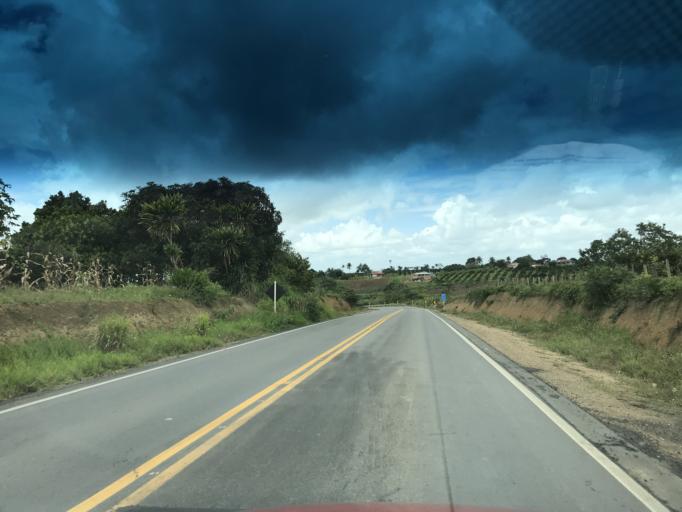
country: BR
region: Bahia
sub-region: Conceicao Do Almeida
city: Conceicao do Almeida
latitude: -12.6974
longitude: -39.2419
